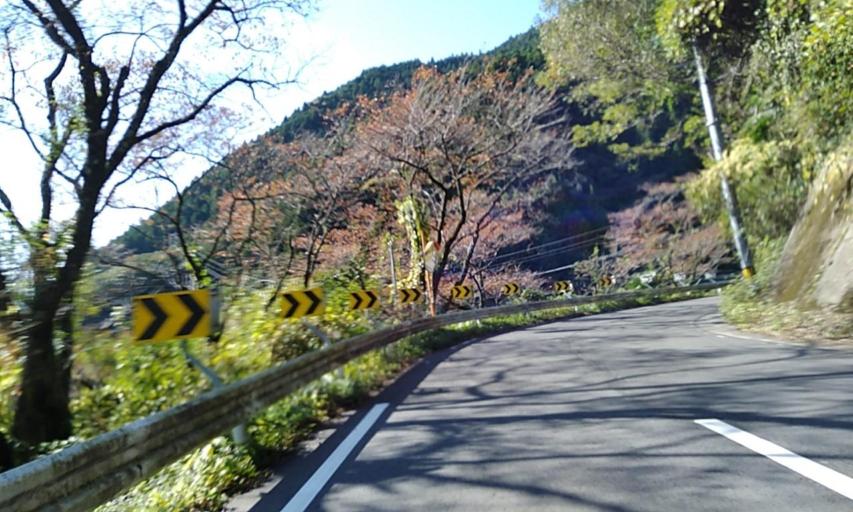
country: JP
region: Wakayama
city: Iwade
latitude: 34.0849
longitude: 135.3574
